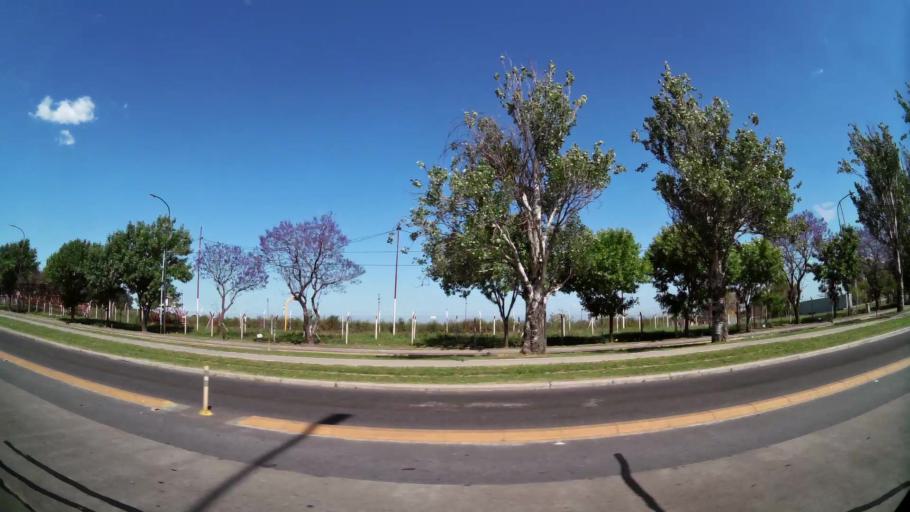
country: AR
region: Buenos Aires F.D.
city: Villa Lugano
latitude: -34.6825
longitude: -58.4532
